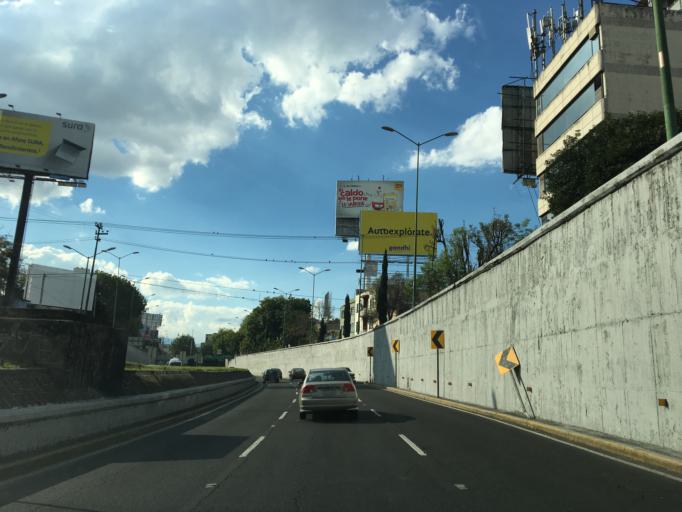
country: MX
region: Mexico City
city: Benito Juarez
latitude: 19.3996
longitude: -99.1776
